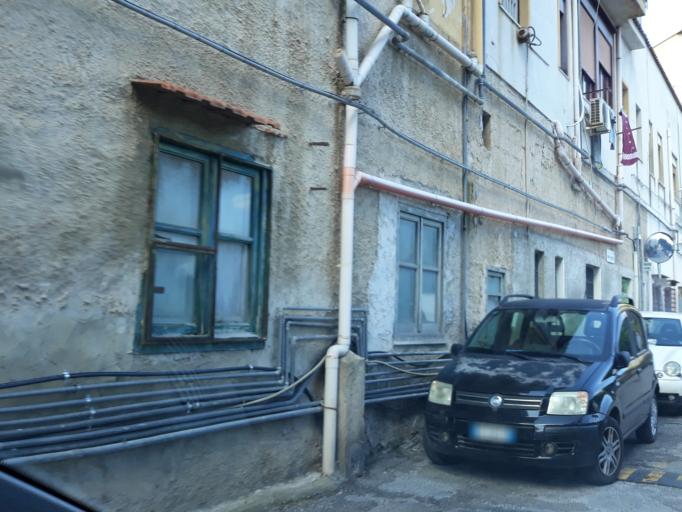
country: IT
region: Sicily
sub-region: Palermo
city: Monreale
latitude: 38.0970
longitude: 13.3132
